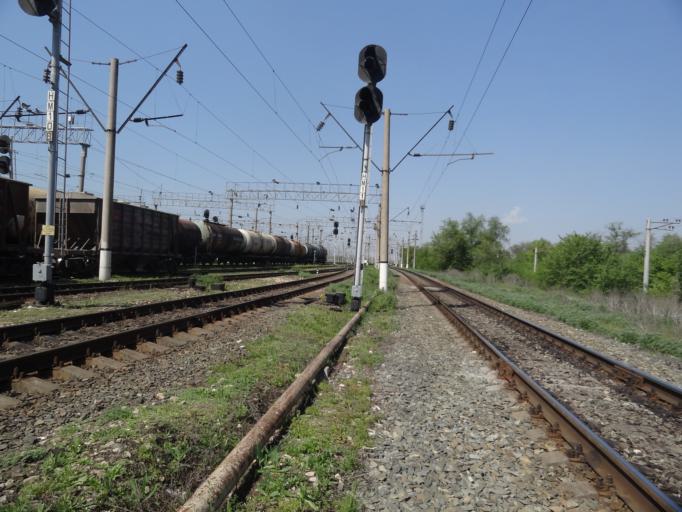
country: RU
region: Saratov
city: Privolzhskiy
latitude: 51.4049
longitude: 46.1059
